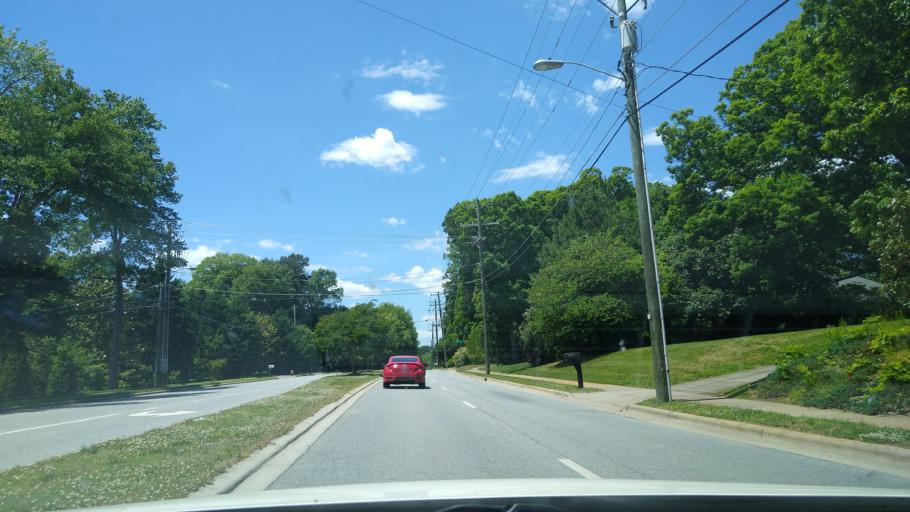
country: US
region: North Carolina
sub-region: Guilford County
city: Greensboro
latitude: 36.0909
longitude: -79.8589
